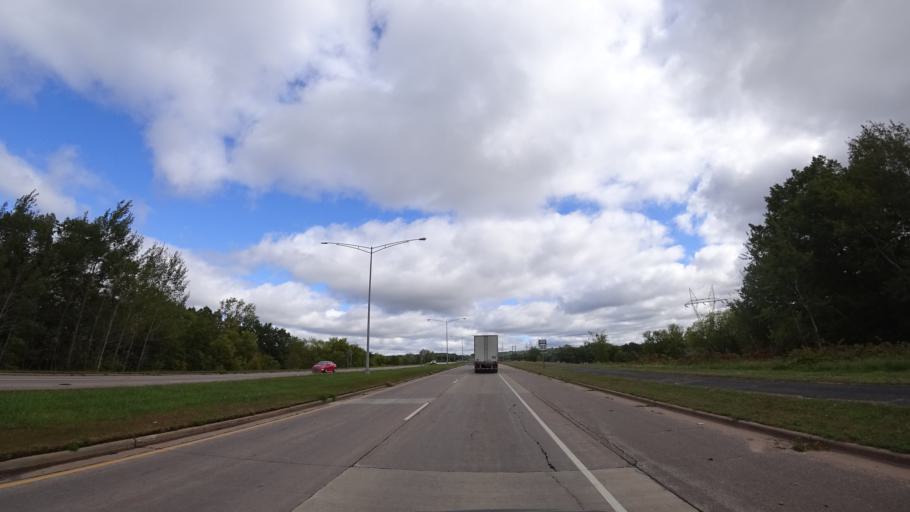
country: US
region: Wisconsin
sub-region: Eau Claire County
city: Eau Claire
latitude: 44.8410
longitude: -91.5046
